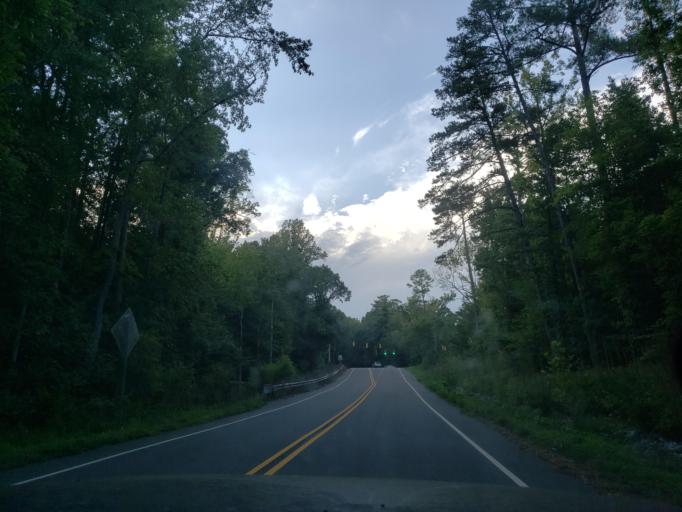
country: US
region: North Carolina
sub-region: Durham County
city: Durham
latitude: 35.9935
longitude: -78.9731
